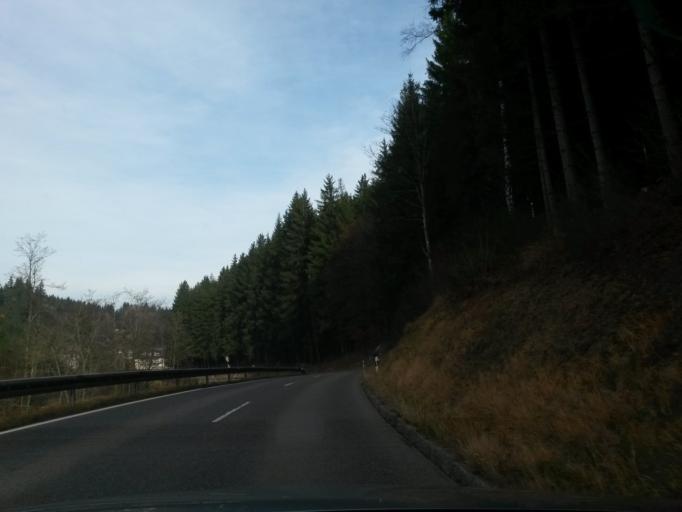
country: DE
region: Baden-Wuerttemberg
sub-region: Freiburg Region
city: Tennenbronn
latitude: 48.1639
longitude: 8.3271
